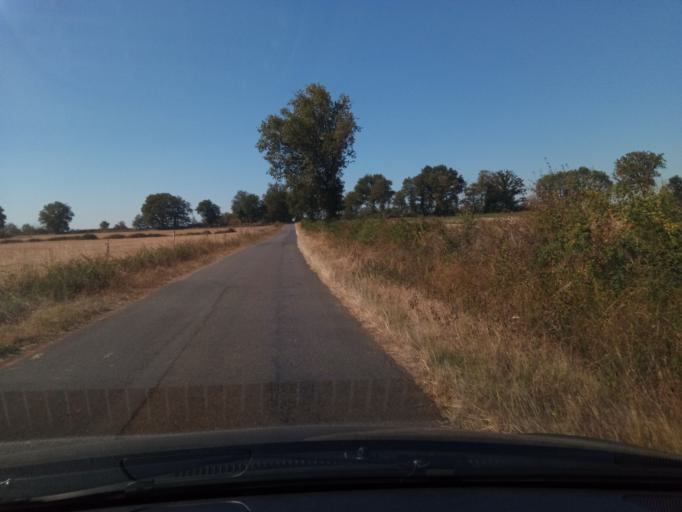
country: FR
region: Poitou-Charentes
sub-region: Departement de la Vienne
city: Montmorillon
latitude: 46.4798
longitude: 0.8678
